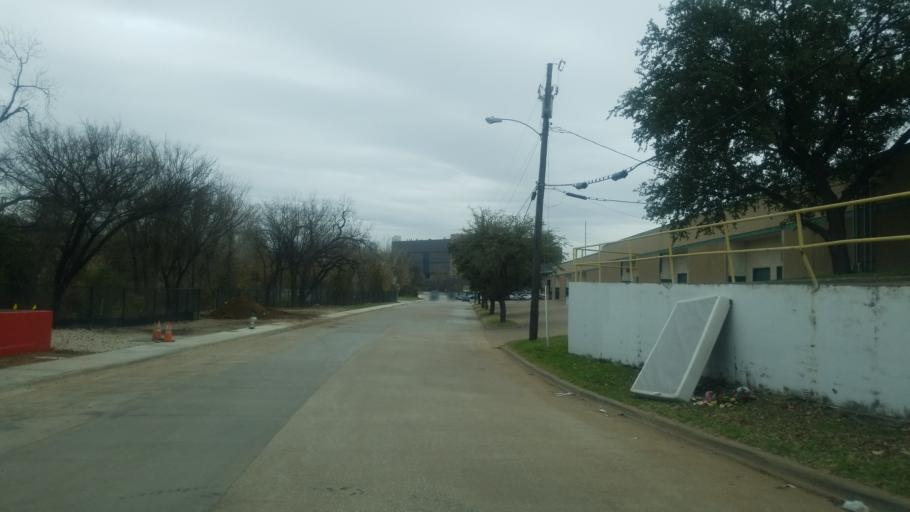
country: US
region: Texas
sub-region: Dallas County
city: Dallas
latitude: 32.8093
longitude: -96.8297
